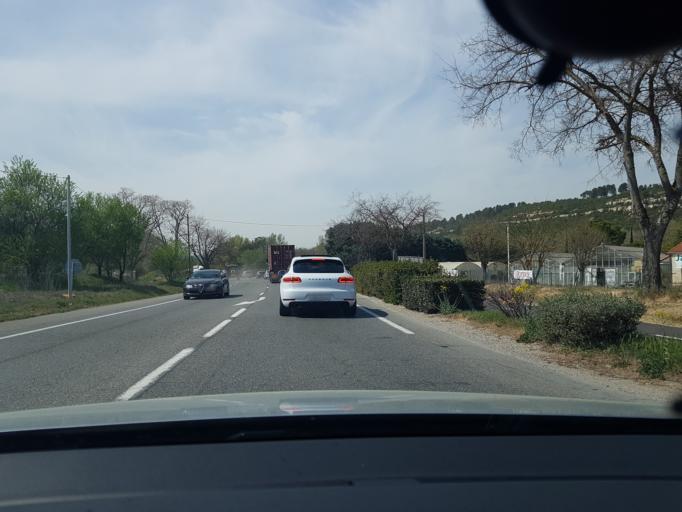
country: FR
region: Provence-Alpes-Cote d'Azur
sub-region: Departement des Bouches-du-Rhone
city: Chateauneuf-le-Rouge
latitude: 43.4790
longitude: 5.5598
